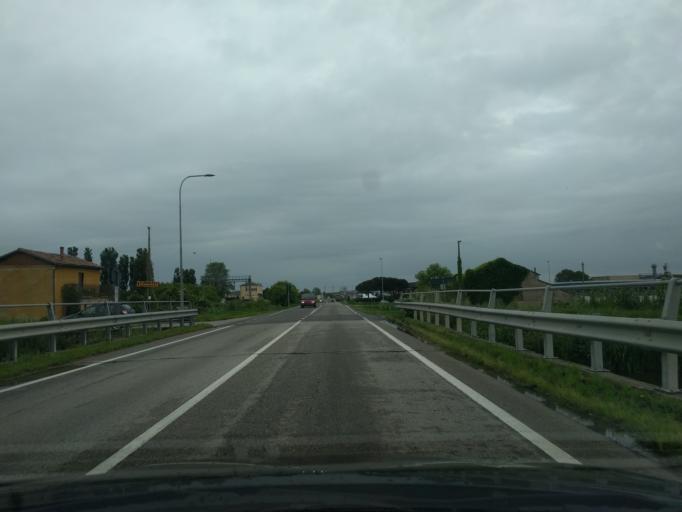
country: IT
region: Veneto
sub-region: Provincia di Rovigo
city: Loreo
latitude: 45.0599
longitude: 12.1874
